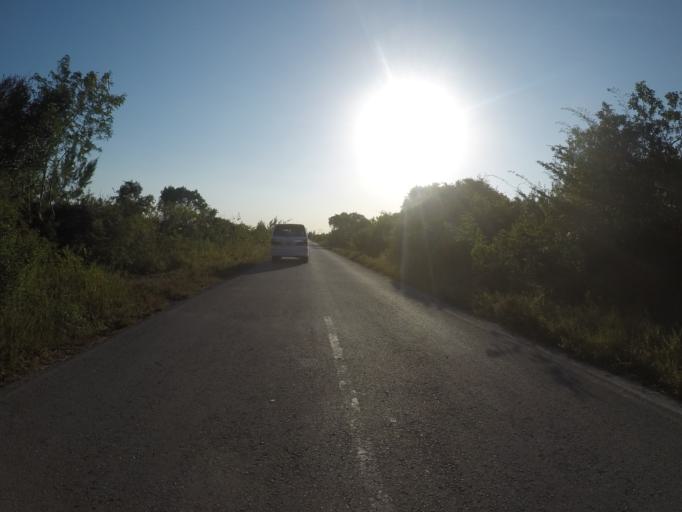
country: TZ
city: Kiwengwa
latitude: -6.1444
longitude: 39.5039
